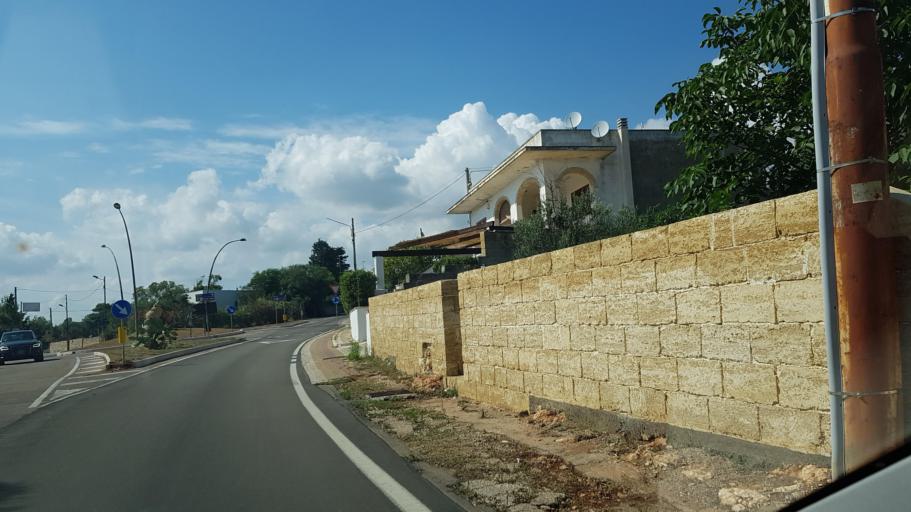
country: IT
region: Apulia
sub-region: Provincia di Lecce
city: Morciano di Leuca
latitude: 39.8145
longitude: 18.3135
